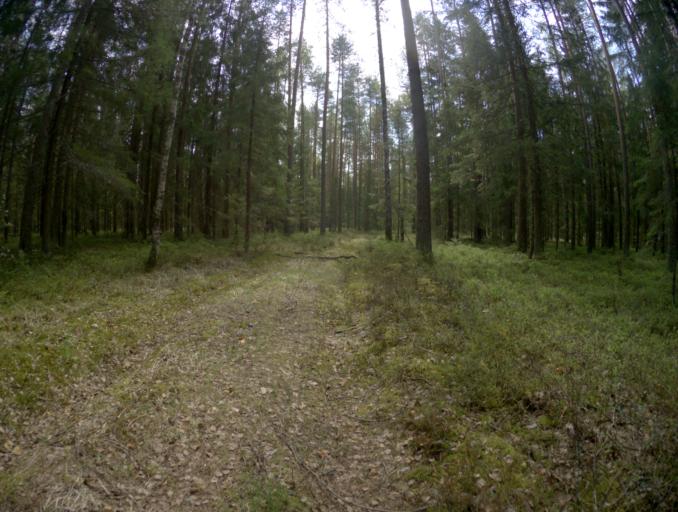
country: RU
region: Vladimir
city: Golovino
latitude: 55.9269
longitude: 40.3662
